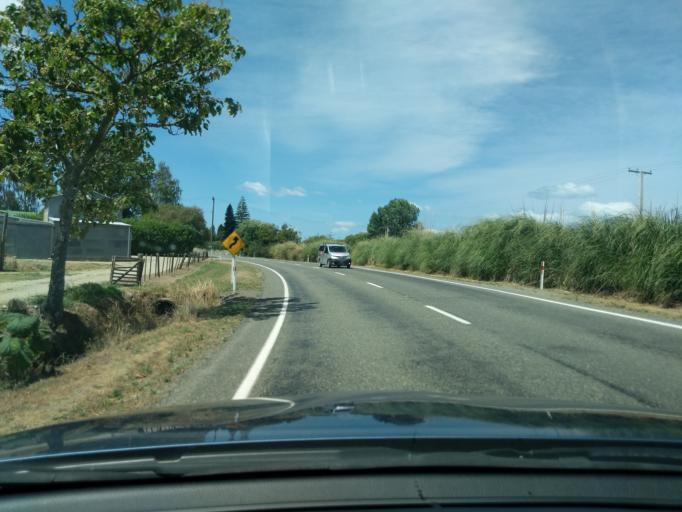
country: NZ
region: Tasman
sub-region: Tasman District
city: Motueka
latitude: -41.0614
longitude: 172.9747
